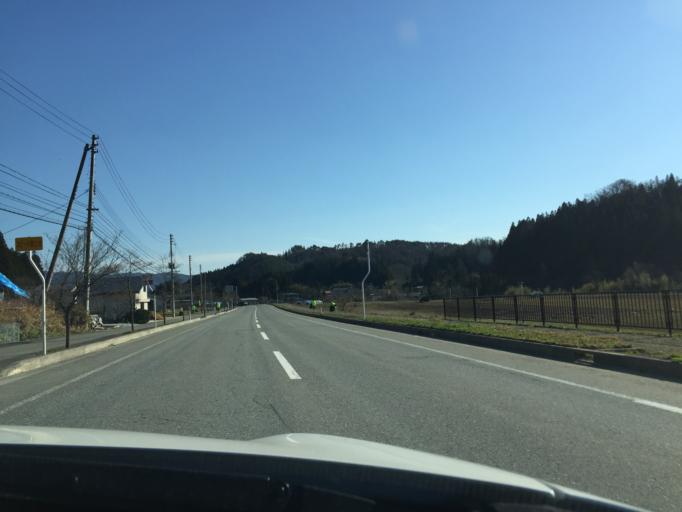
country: JP
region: Yamagata
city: Nagai
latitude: 38.2164
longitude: 140.0988
